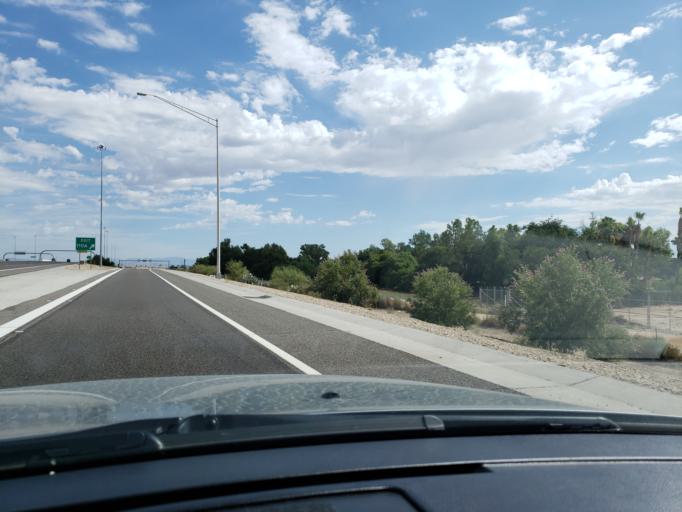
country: US
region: Arizona
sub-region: Maricopa County
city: Citrus Park
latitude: 33.5476
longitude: -112.4179
